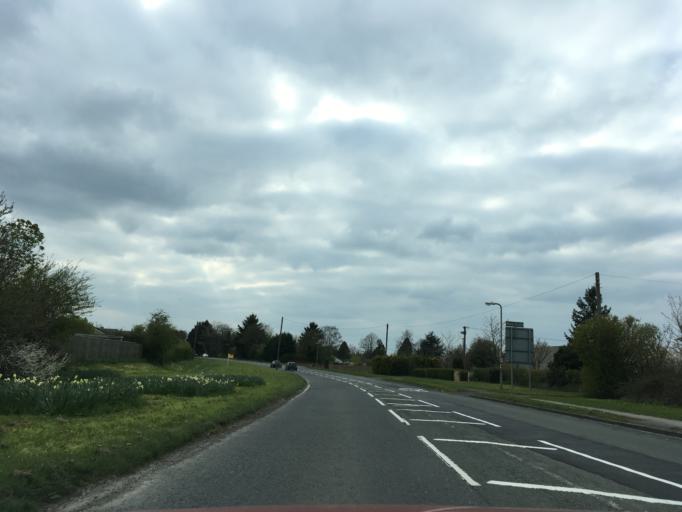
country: GB
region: England
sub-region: Oxfordshire
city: Carterton
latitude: 51.7971
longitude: -1.5463
